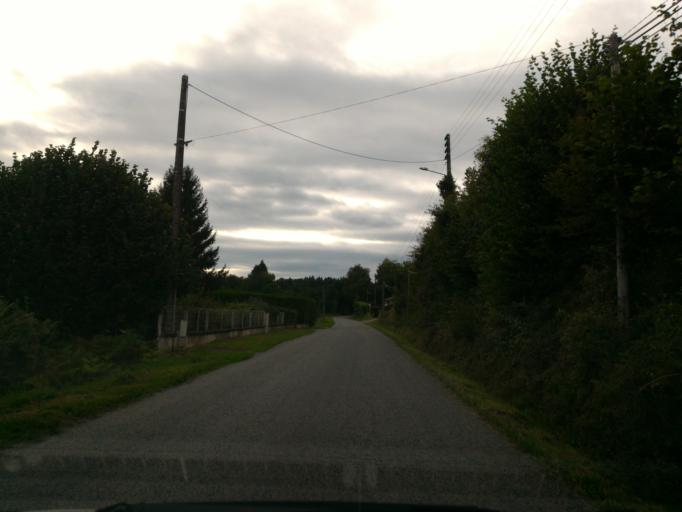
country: FR
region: Limousin
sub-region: Departement de la Haute-Vienne
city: Saint-Junien
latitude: 45.8962
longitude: 0.8791
